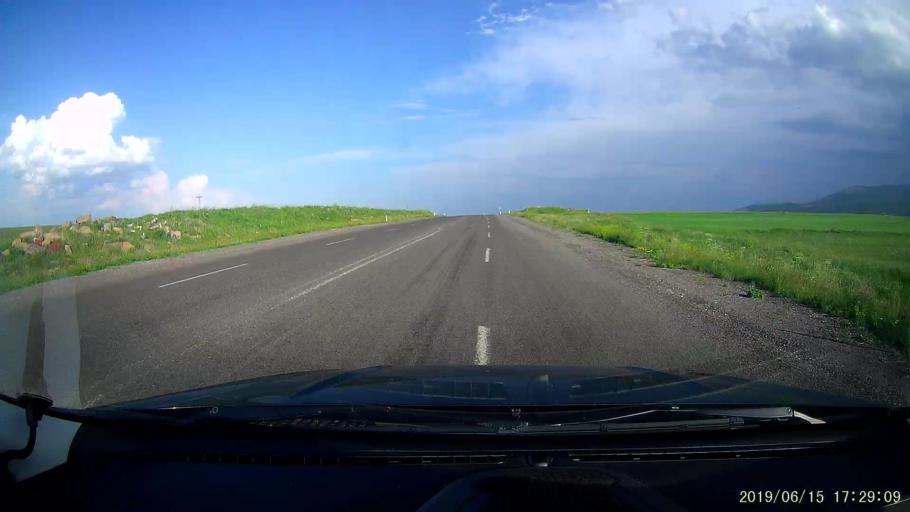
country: TR
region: Kars
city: Basgedikler
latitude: 40.5917
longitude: 43.4492
